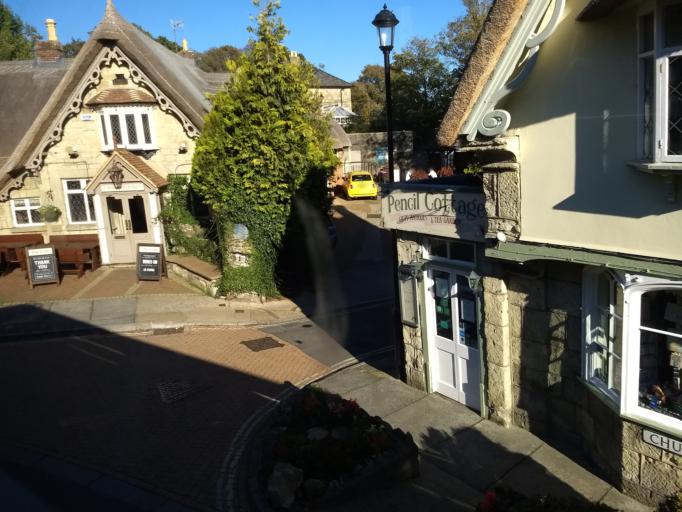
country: GB
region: England
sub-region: Isle of Wight
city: Shanklin
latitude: 50.6255
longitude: -1.1784
